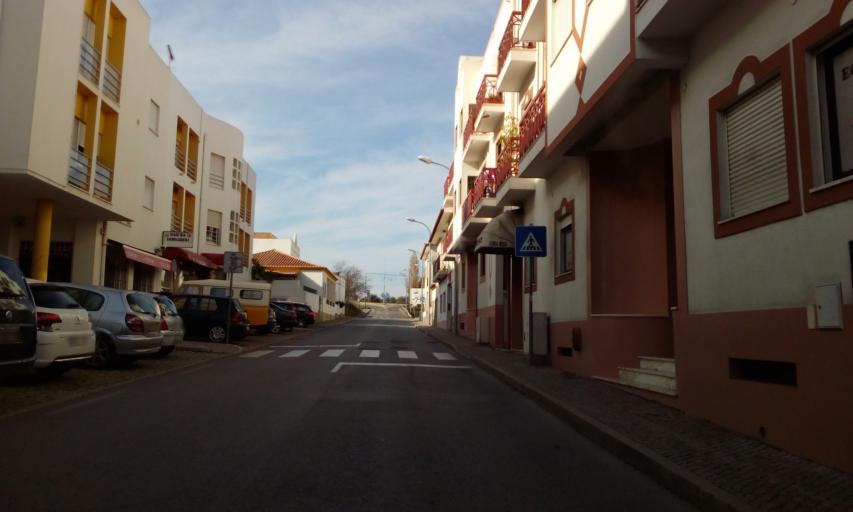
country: PT
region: Faro
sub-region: Tavira
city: Tavira
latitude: 37.1246
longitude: -7.6566
